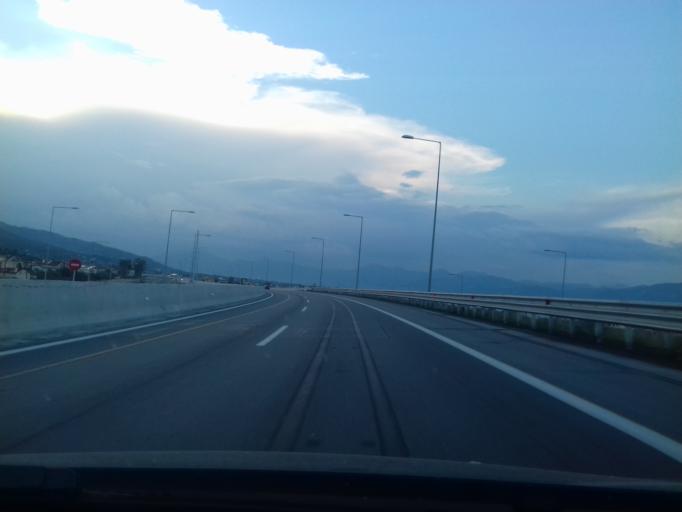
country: GR
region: West Greece
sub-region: Nomos Achaias
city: Aigio
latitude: 38.2629
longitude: 22.0591
